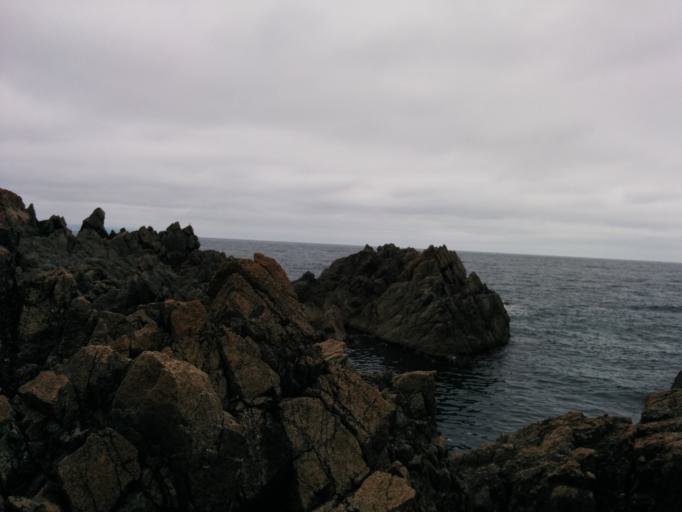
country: JP
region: Hokkaido
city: Iwanai
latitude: 42.3066
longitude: 139.7670
